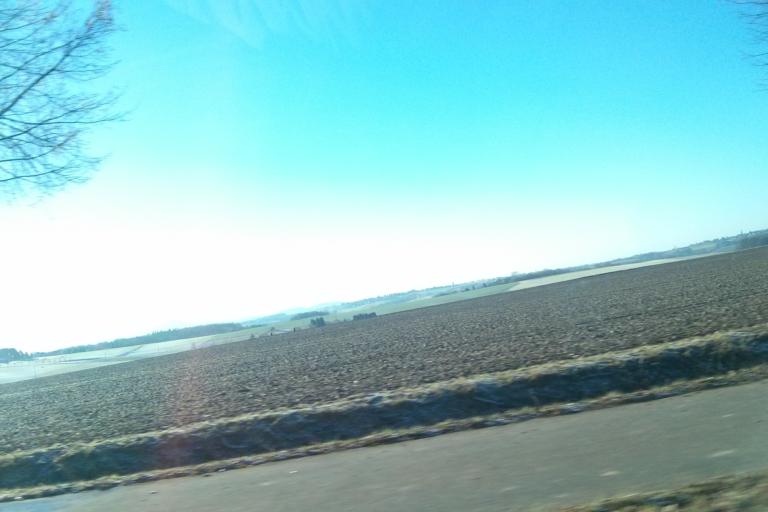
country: DE
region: North Rhine-Westphalia
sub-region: Regierungsbezirk Koln
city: Hennef
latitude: 50.7507
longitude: 7.3409
